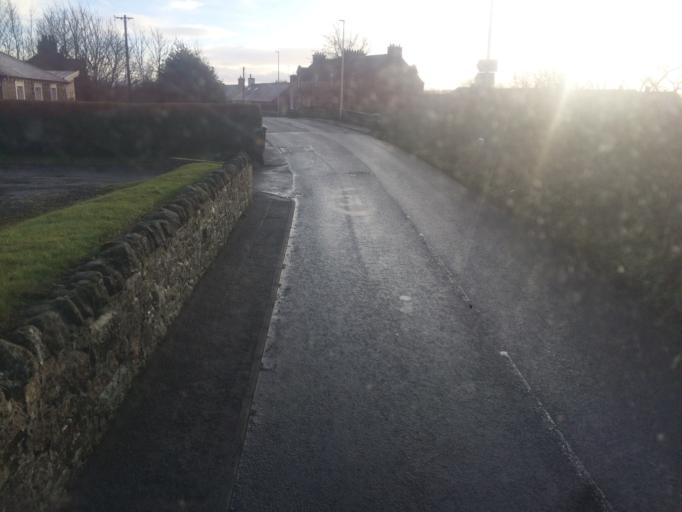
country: GB
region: Scotland
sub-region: Midlothian
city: Loanhead
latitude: 55.8606
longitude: -3.1689
